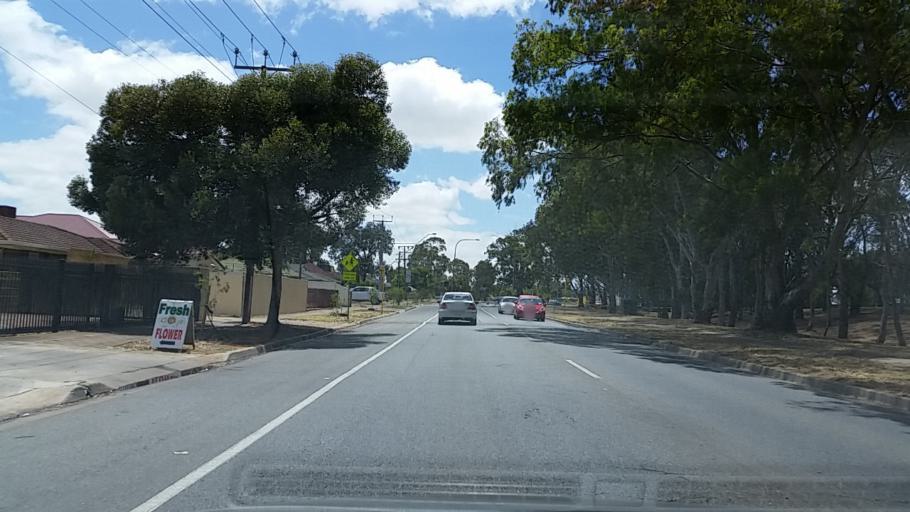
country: AU
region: South Australia
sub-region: Salisbury
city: Salisbury
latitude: -34.7697
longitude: 138.6190
